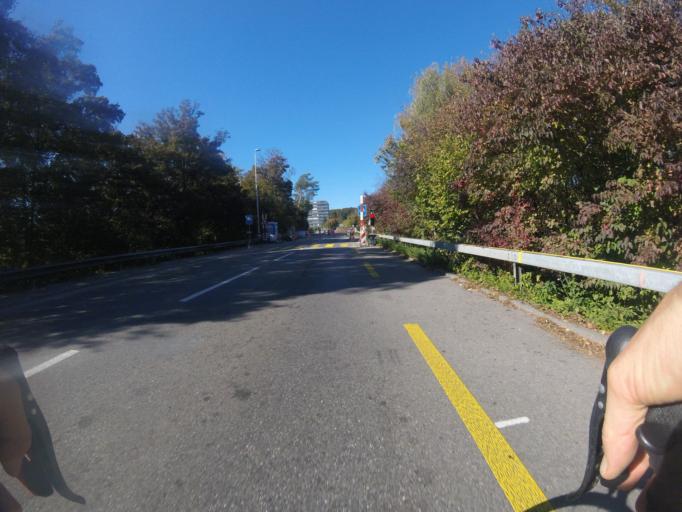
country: CH
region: Bern
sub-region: Bern-Mittelland District
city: Wohlen
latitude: 46.9643
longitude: 7.3824
